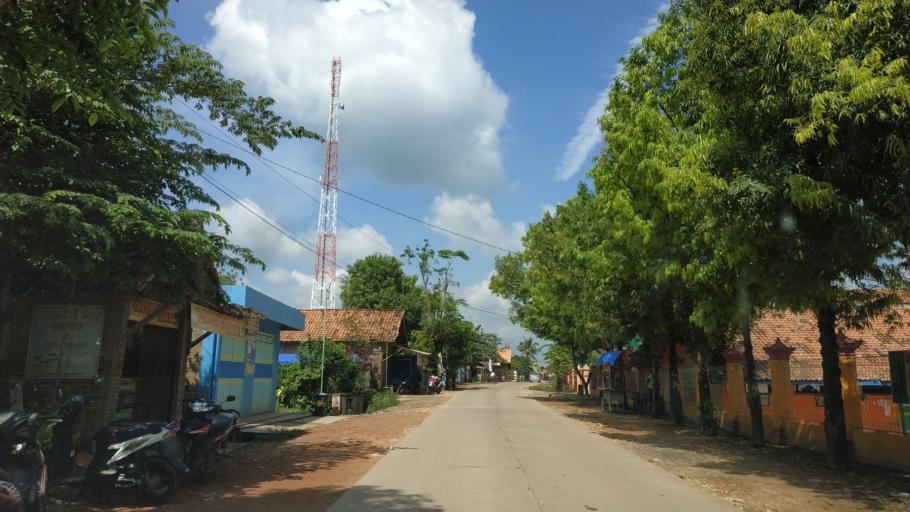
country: ID
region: Central Java
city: Jepang
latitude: -7.0090
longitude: 111.1152
